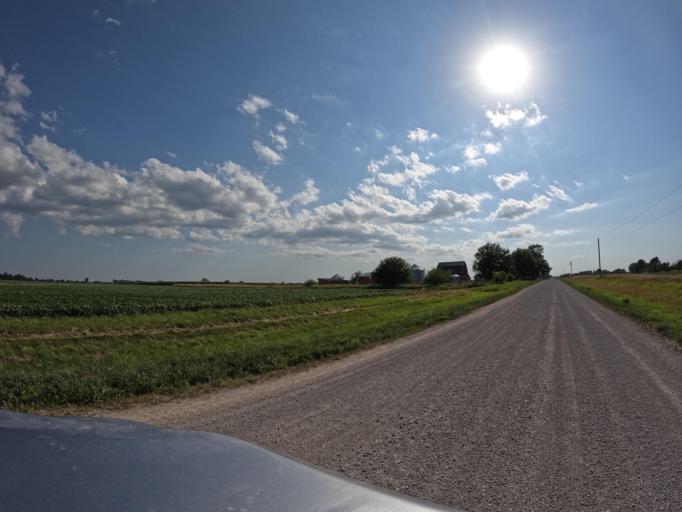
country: US
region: Iowa
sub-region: Appanoose County
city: Centerville
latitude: 40.7179
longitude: -93.0418
